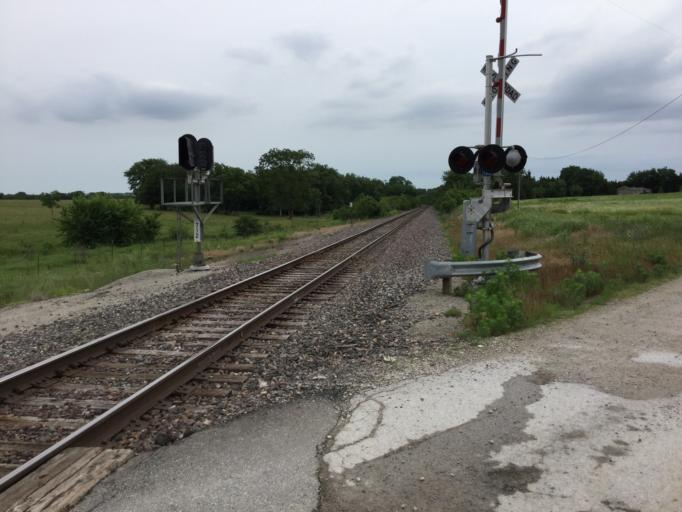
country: US
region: Kansas
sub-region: Anderson County
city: Garnett
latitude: 38.2046
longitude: -95.0336
